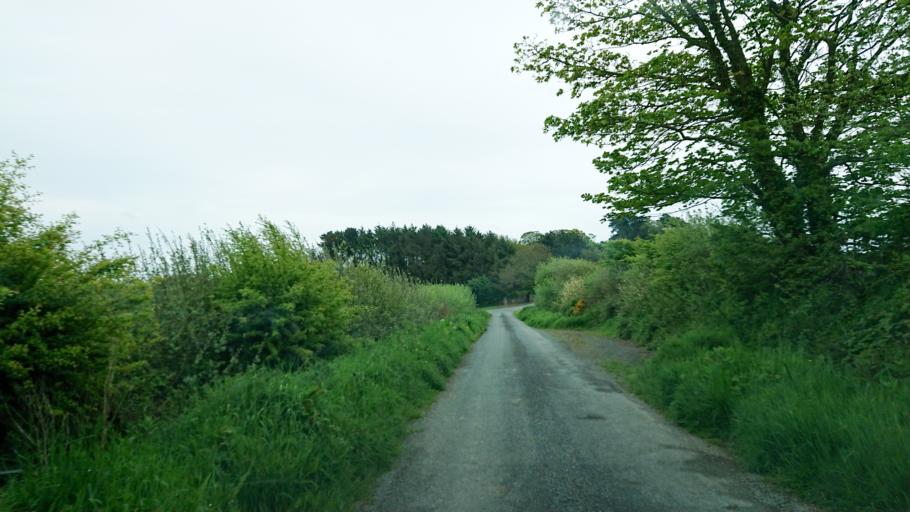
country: IE
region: Munster
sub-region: Waterford
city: Dunmore East
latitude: 52.2220
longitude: -7.0138
